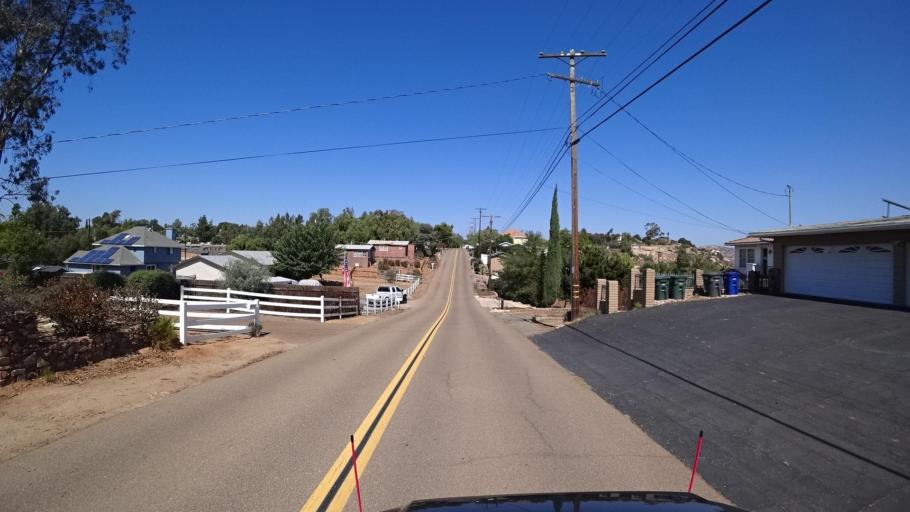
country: US
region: California
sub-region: San Diego County
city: Crest
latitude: 32.8032
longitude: -116.8645
